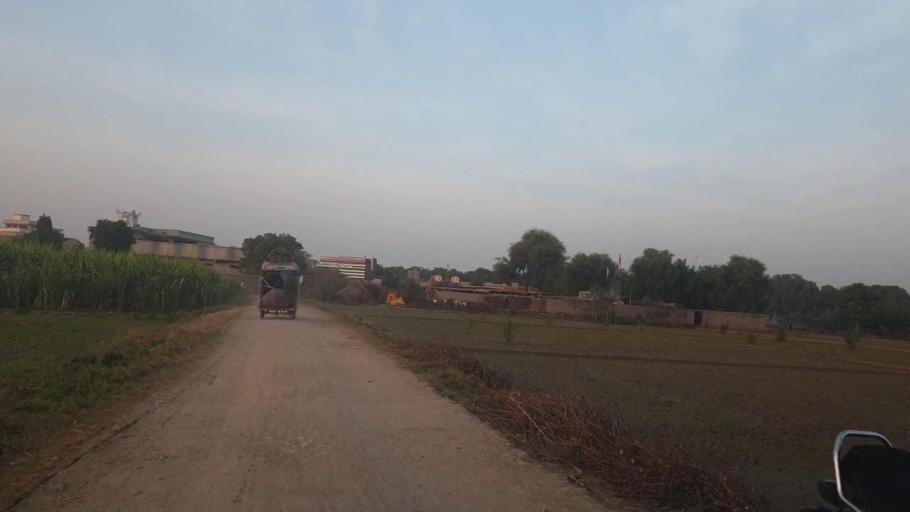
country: PK
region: Sindh
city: Tando Jam
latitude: 25.3834
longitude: 68.5720
